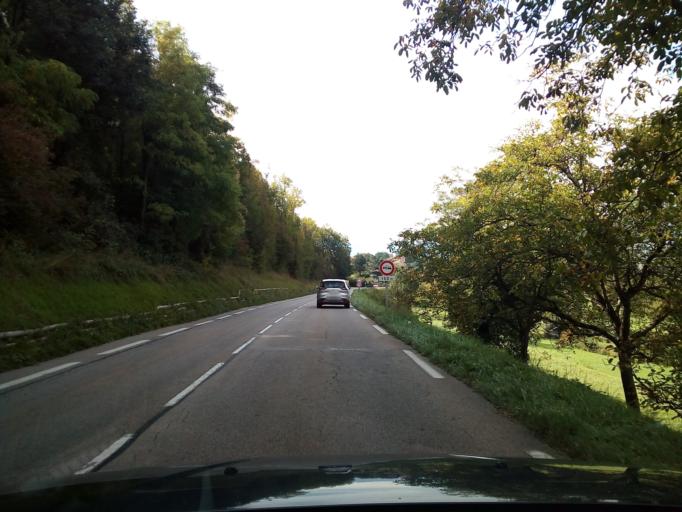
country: FR
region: Rhone-Alpes
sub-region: Departement de l'Isere
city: Goncelin
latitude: 45.3482
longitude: 5.9859
